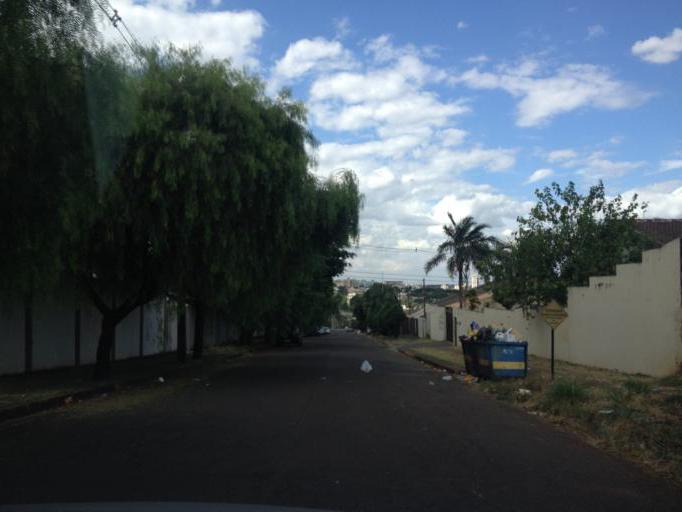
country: BR
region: Parana
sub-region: Maringa
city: Maringa
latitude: -23.4464
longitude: -51.9473
